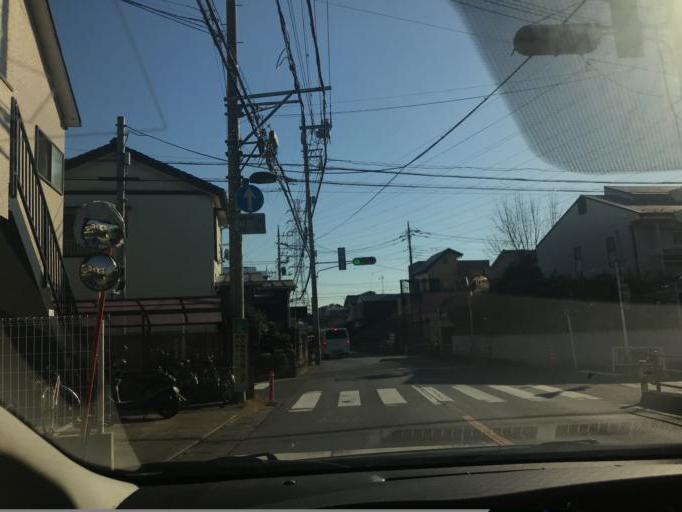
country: JP
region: Saitama
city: Yashio-shi
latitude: 35.8354
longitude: 139.8361
